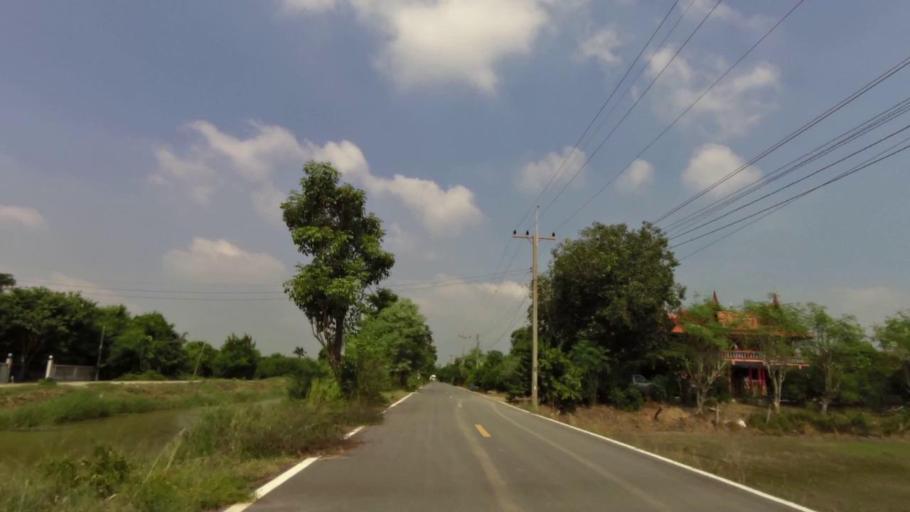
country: TH
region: Ang Thong
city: Ang Thong
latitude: 14.6061
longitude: 100.3994
